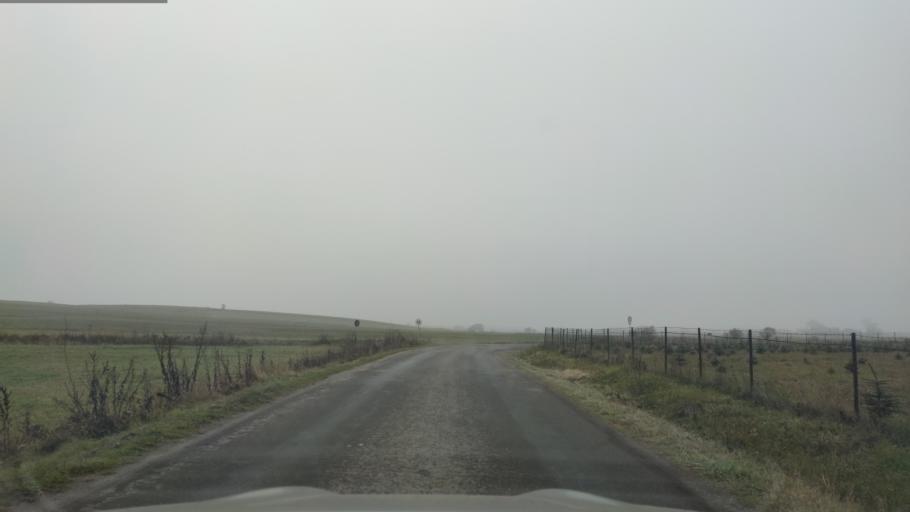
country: RO
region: Harghita
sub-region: Comuna Remetea
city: Remetea
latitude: 46.8040
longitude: 25.4325
